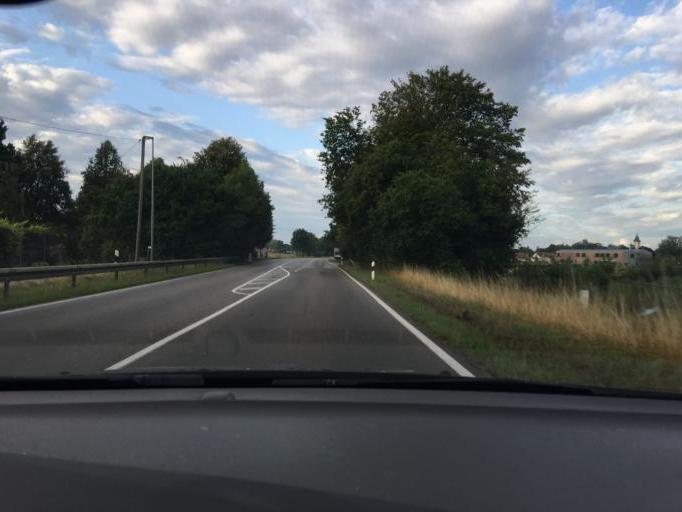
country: DE
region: Bavaria
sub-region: Upper Bavaria
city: Erding
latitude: 48.2998
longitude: 11.9150
